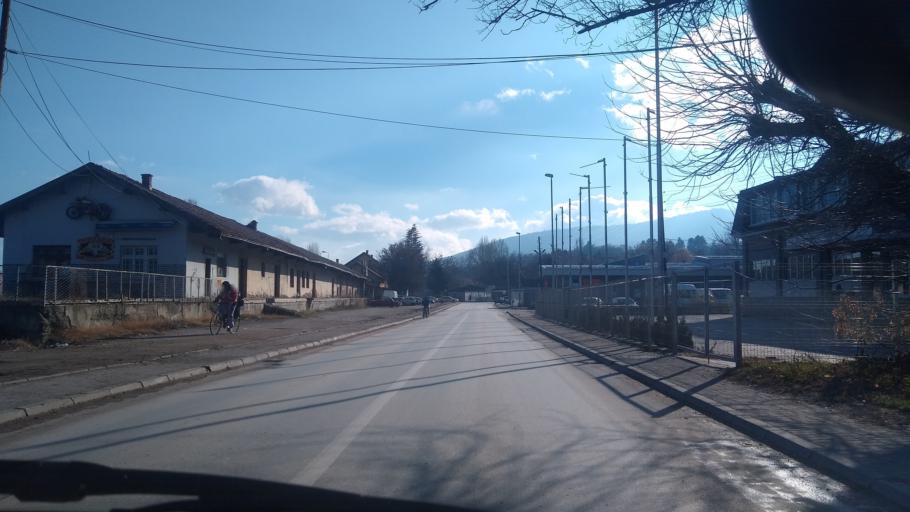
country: MK
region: Bitola
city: Bitola
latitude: 41.0211
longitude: 21.3423
